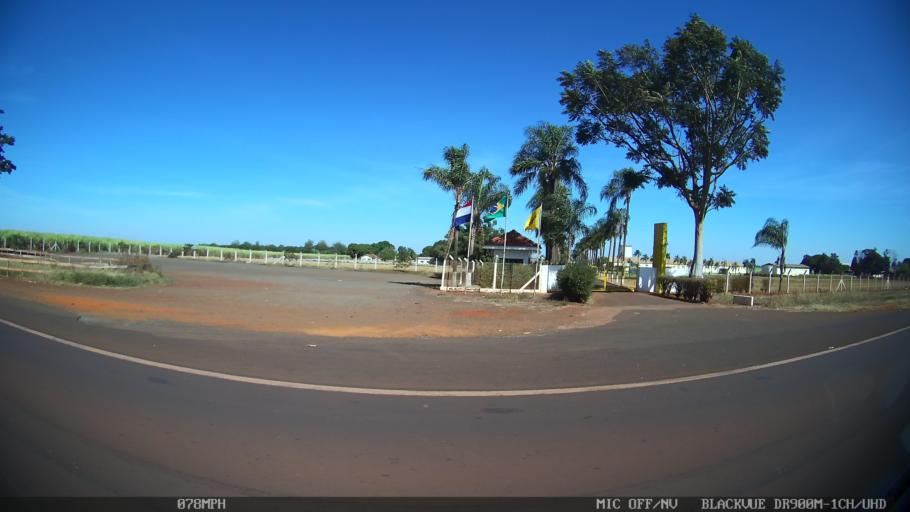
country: BR
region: Sao Paulo
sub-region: Guaira
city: Guaira
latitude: -20.4444
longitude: -48.2884
